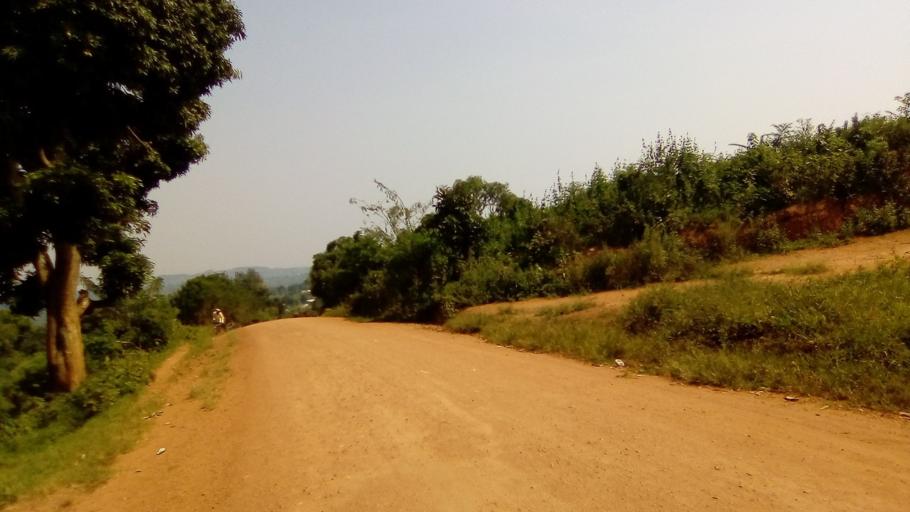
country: UG
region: Central Region
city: Masaka
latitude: -0.2721
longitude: 31.6451
